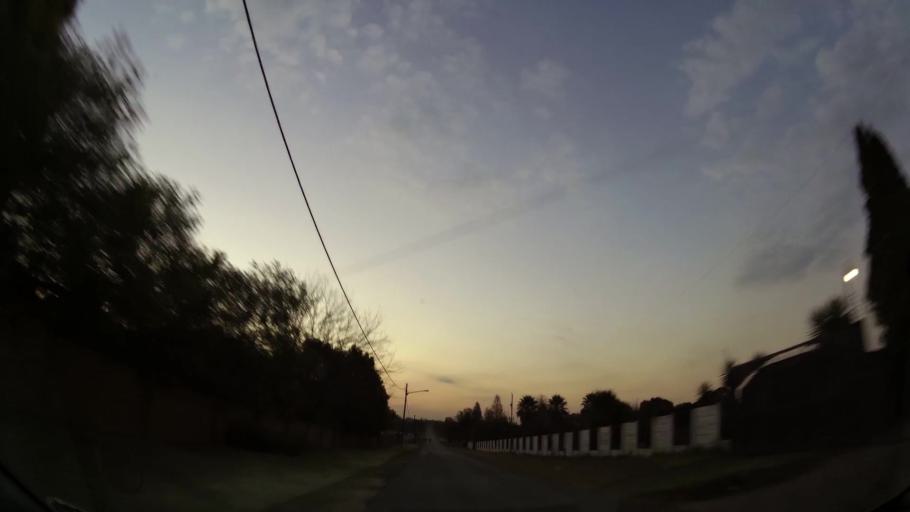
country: ZA
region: Gauteng
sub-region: Ekurhuleni Metropolitan Municipality
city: Benoni
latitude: -26.1300
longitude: 28.3102
